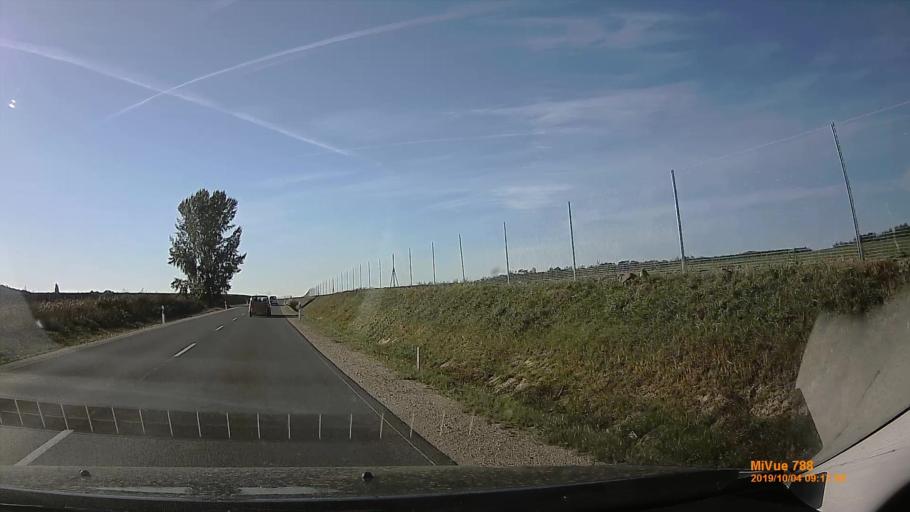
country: HU
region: Somogy
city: Karad
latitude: 46.5980
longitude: 17.8008
